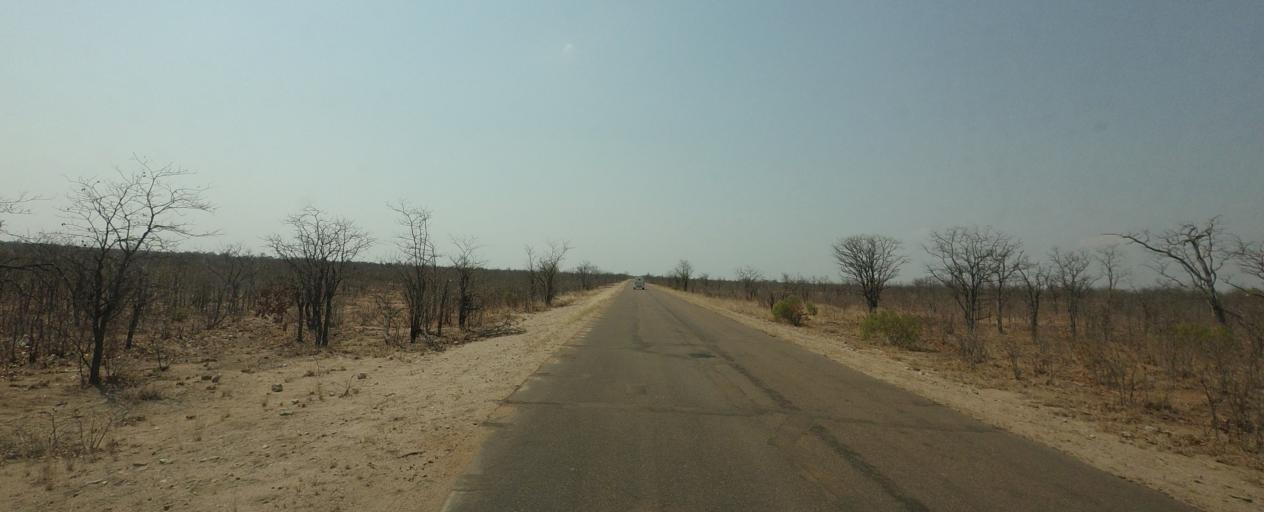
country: ZA
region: Limpopo
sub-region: Mopani District Municipality
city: Giyani
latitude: -23.3618
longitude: 31.3194
